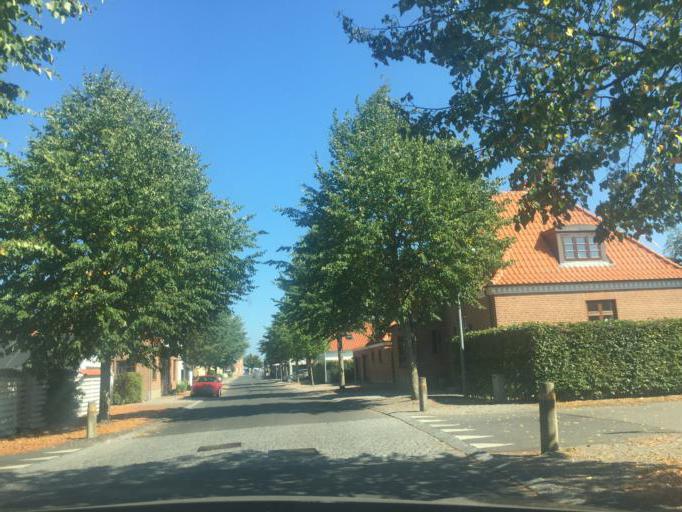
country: DK
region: Central Jutland
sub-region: Hedensted Kommune
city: Juelsminde
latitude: 55.7134
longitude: 10.0094
